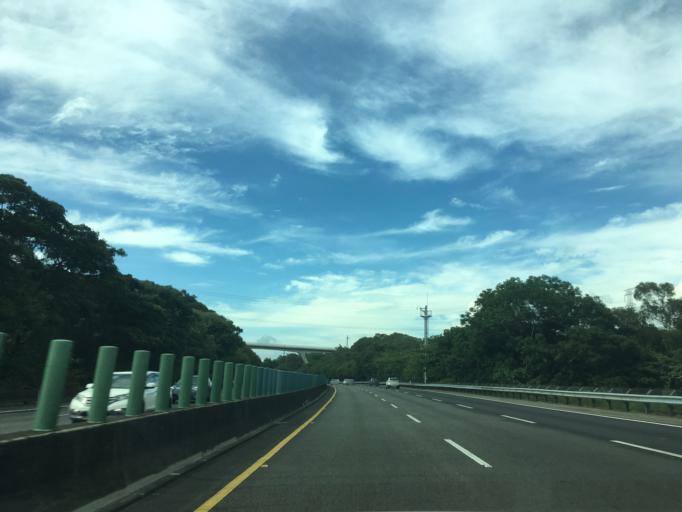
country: TW
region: Taiwan
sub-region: Chiayi
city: Jiayi Shi
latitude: 23.5453
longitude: 120.5028
